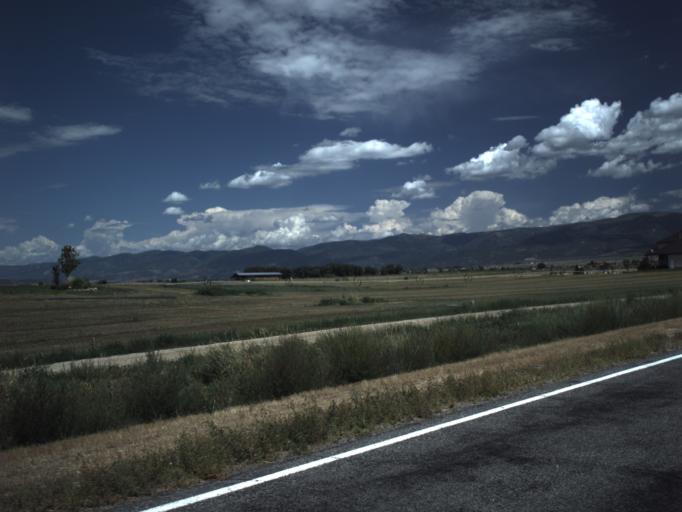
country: US
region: Utah
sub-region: Sanpete County
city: Moroni
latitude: 39.4810
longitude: -111.5306
